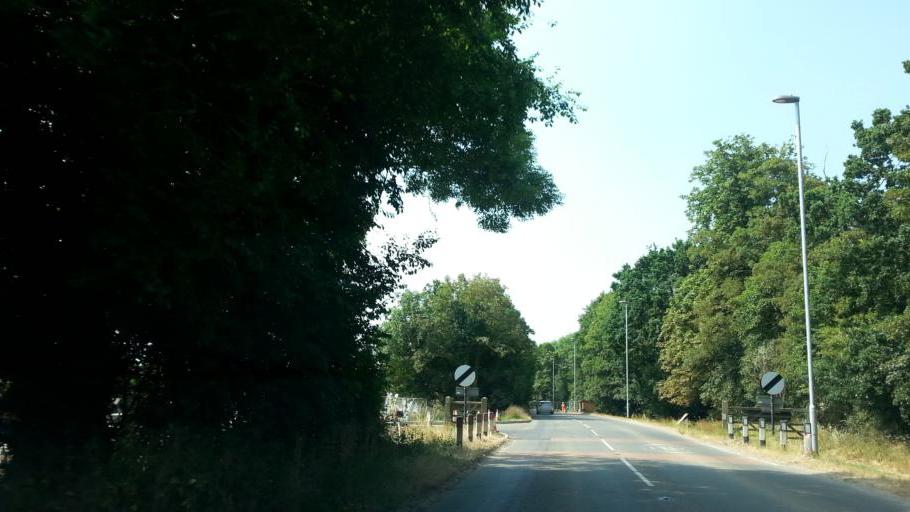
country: GB
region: England
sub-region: Cambridgeshire
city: Brampton
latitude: 52.3151
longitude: -0.2232
